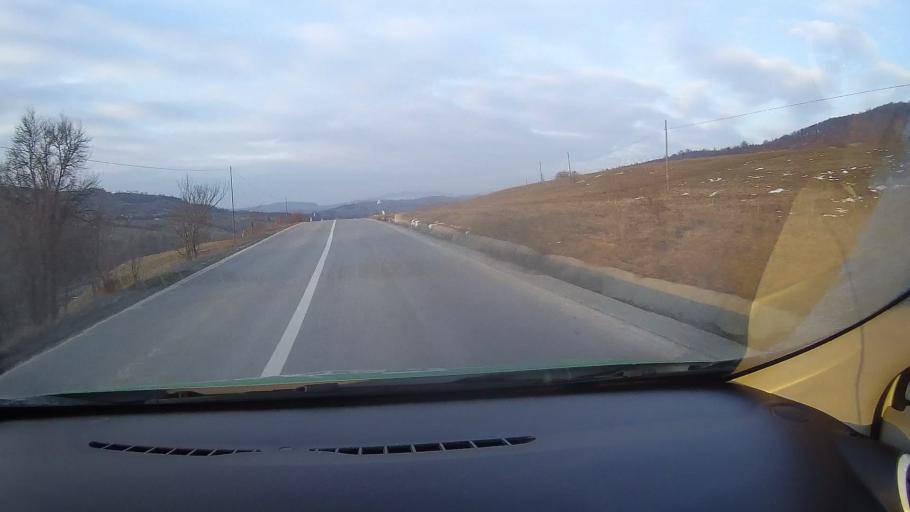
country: RO
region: Harghita
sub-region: Comuna Simonesti
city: Simonesti
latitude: 46.3210
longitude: 25.0994
